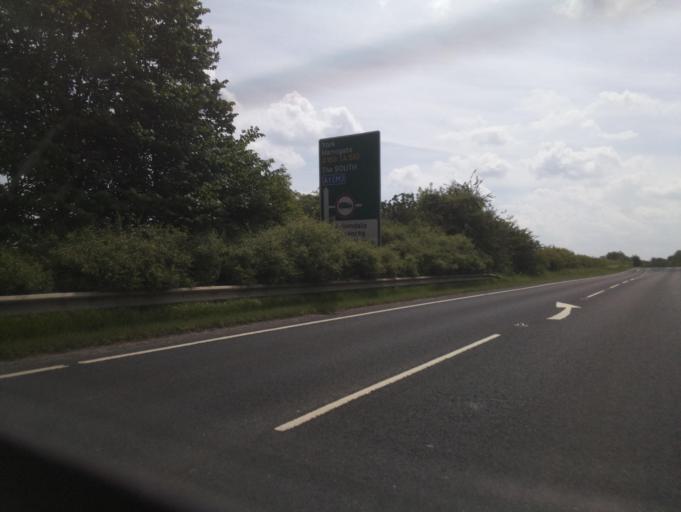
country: GB
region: England
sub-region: North Yorkshire
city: Boroughbridge
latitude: 54.0514
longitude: -1.3871
